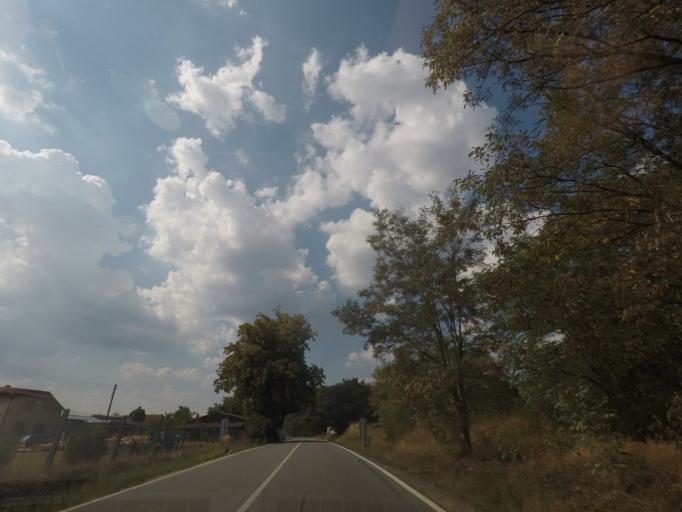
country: CZ
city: Albrechtice nad Orlici
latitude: 50.1305
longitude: 16.0629
